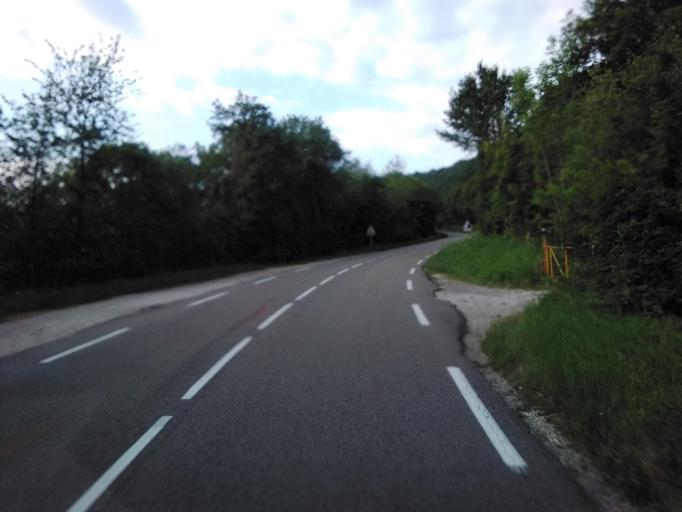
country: FR
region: Franche-Comte
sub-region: Departement du Jura
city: Arbois
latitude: 46.8784
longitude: 5.8014
